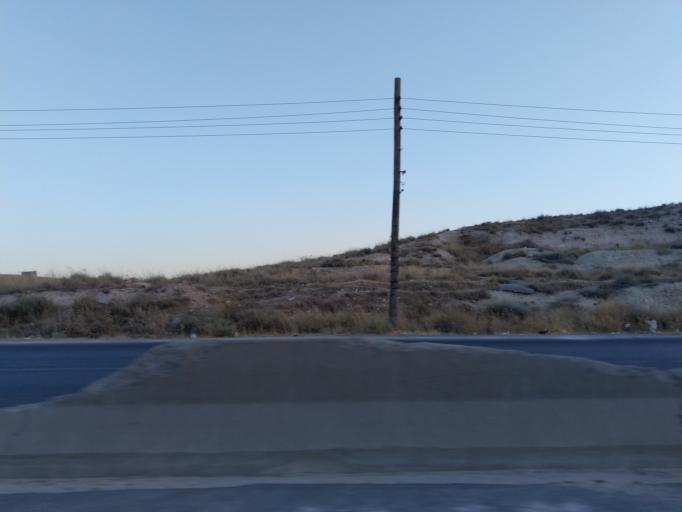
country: SY
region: Rif-dimashq
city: At Tall
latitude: 33.5857
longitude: 36.3021
